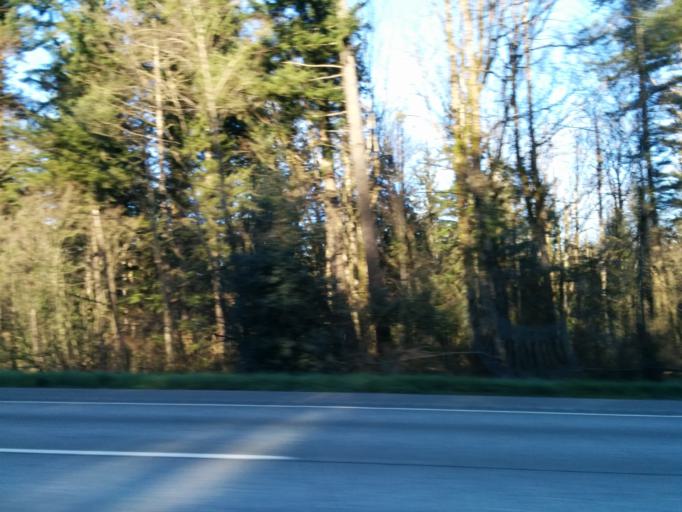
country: US
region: Washington
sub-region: King County
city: Snoqualmie
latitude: 47.5104
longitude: -121.8299
